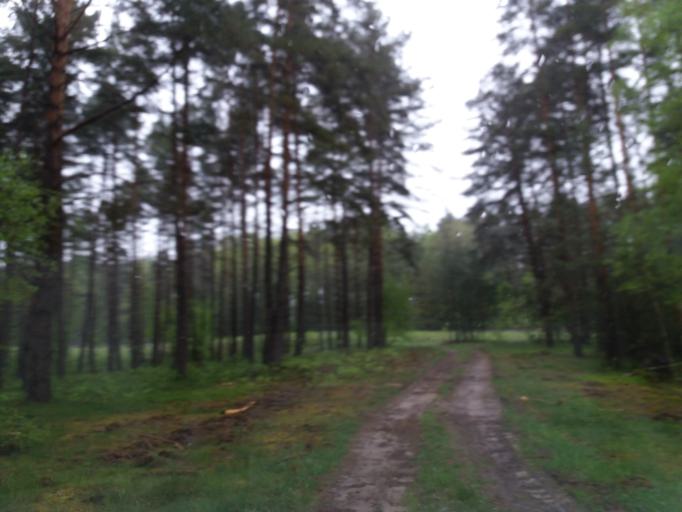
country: PL
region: West Pomeranian Voivodeship
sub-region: Powiat drawski
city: Kalisz Pomorski
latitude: 53.2422
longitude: 16.0138
